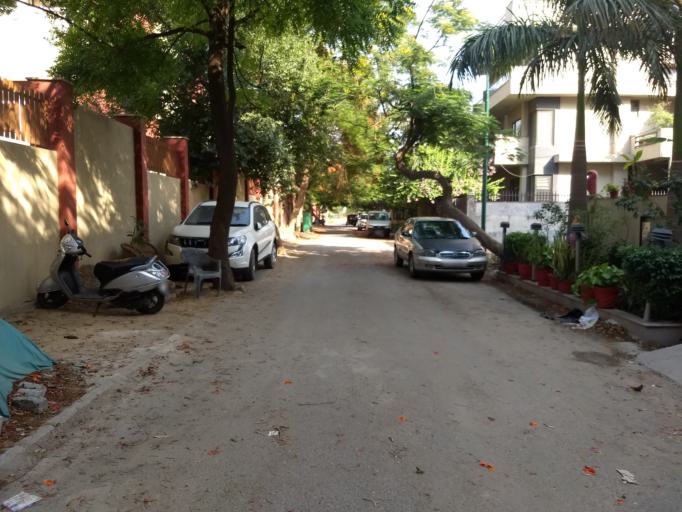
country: IN
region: Haryana
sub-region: Gurgaon
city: Gurgaon
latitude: 28.4436
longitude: 77.0598
